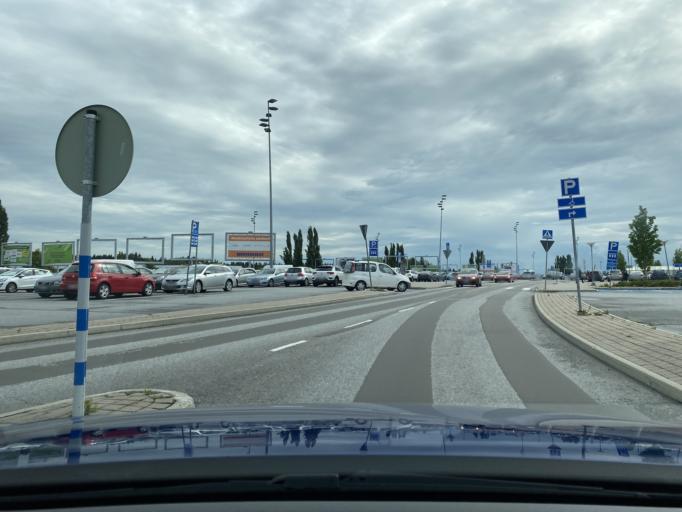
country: FI
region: Pirkanmaa
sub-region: Tampere
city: Lempaeaelae
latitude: 61.3599
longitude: 23.7978
